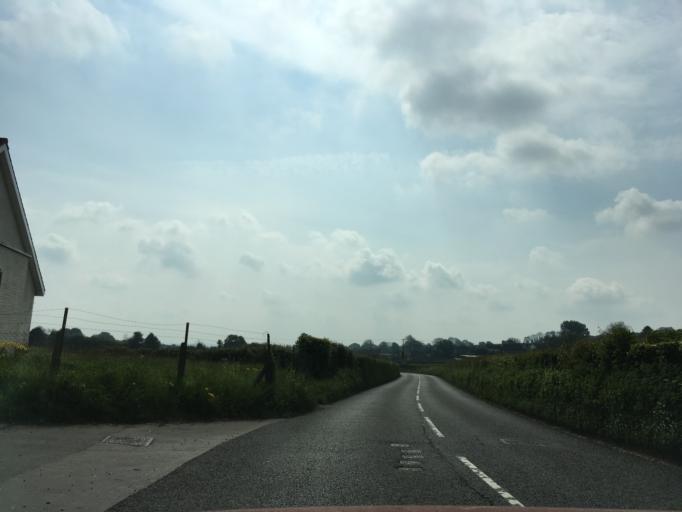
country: GB
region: England
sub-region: North Somerset
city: Winford
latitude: 51.3881
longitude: -2.6941
